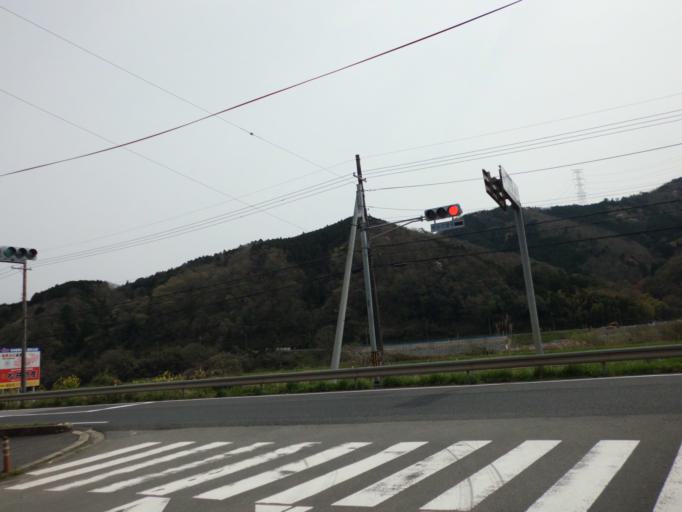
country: JP
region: Kyoto
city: Fukuchiyama
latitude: 35.3574
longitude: 135.1128
